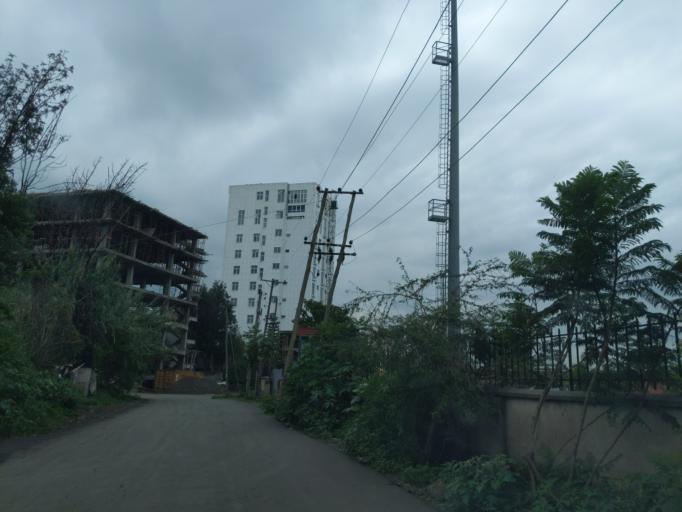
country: ET
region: Adis Abeba
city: Addis Ababa
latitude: 8.9919
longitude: 38.7893
